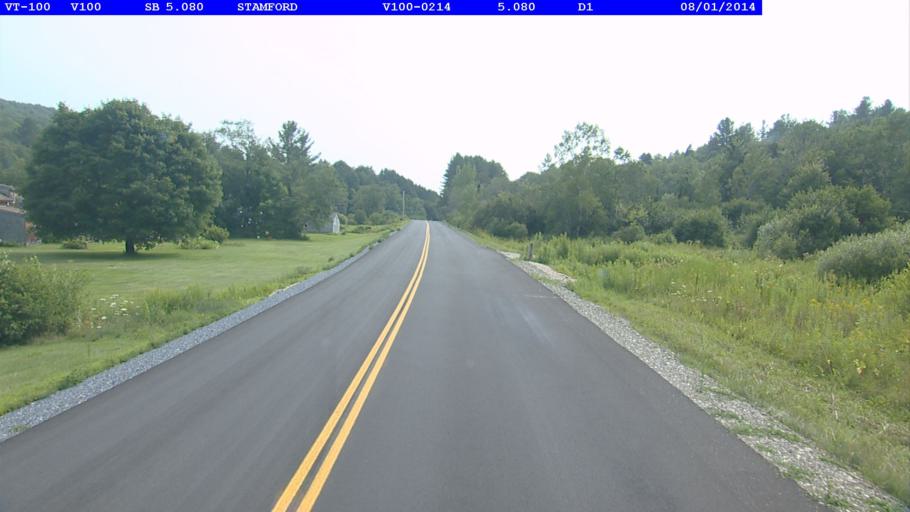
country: US
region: Massachusetts
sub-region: Berkshire County
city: North Adams
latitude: 42.8012
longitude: -73.0229
